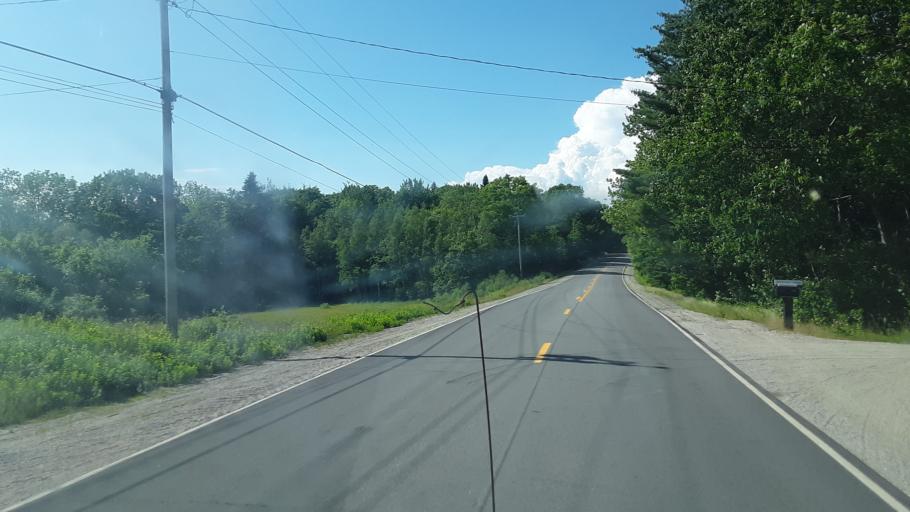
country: US
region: Maine
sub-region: Washington County
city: Cherryfield
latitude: 44.6250
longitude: -67.9377
